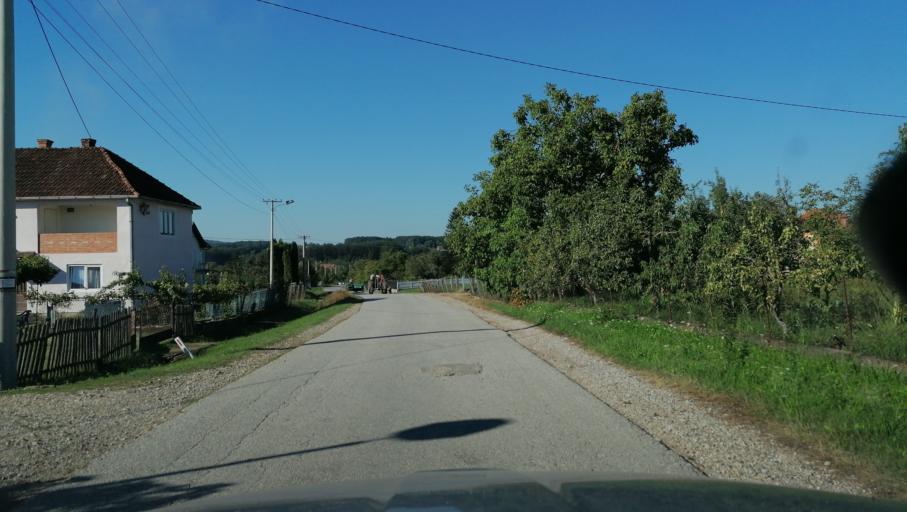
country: RS
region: Central Serbia
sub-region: Sumadijski Okrug
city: Knic
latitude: 43.8783
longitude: 20.6125
